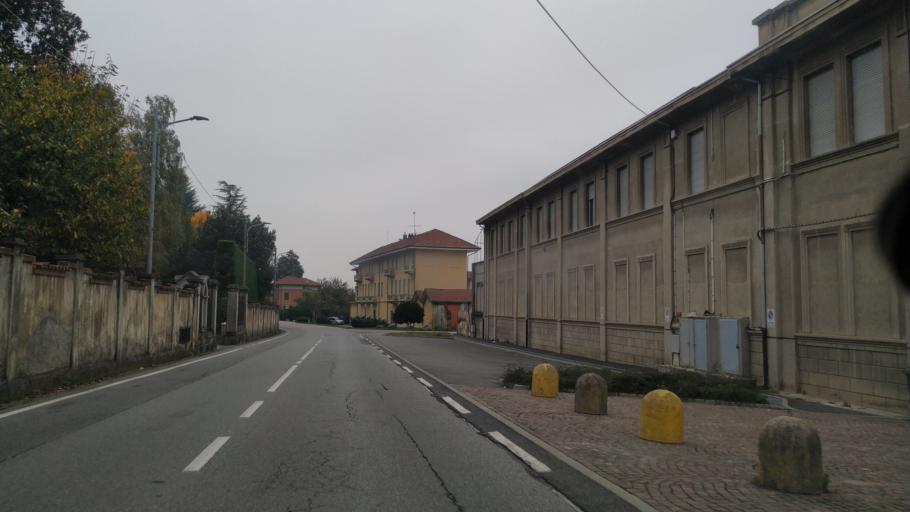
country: IT
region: Piedmont
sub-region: Provincia di Biella
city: Cossato
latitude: 45.5731
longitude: 8.1861
